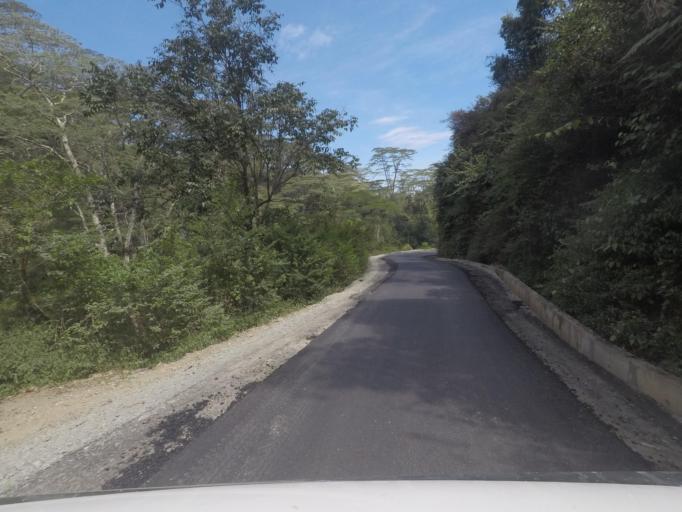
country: TL
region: Ermera
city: Gleno
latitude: -8.7532
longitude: 125.3354
